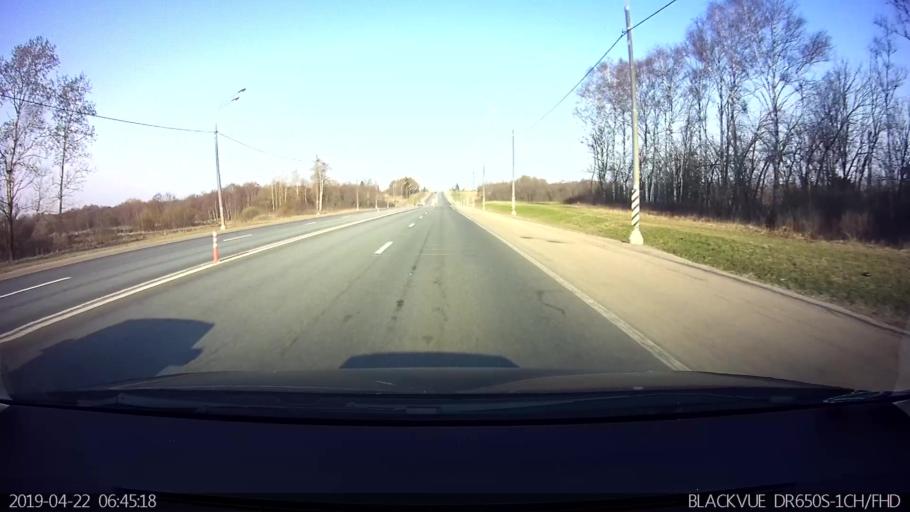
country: RU
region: Smolensk
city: Gagarin
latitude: 55.5040
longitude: 35.1408
